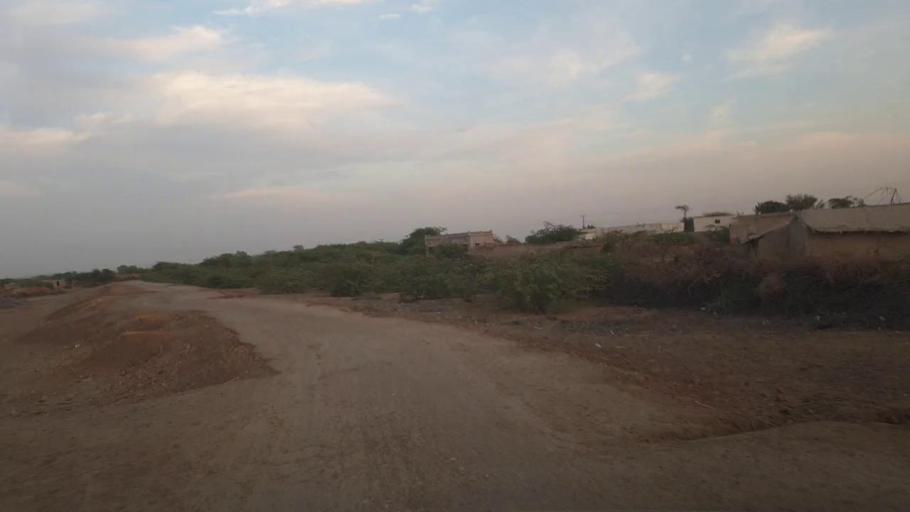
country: PK
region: Sindh
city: Umarkot
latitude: 25.2656
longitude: 69.6697
